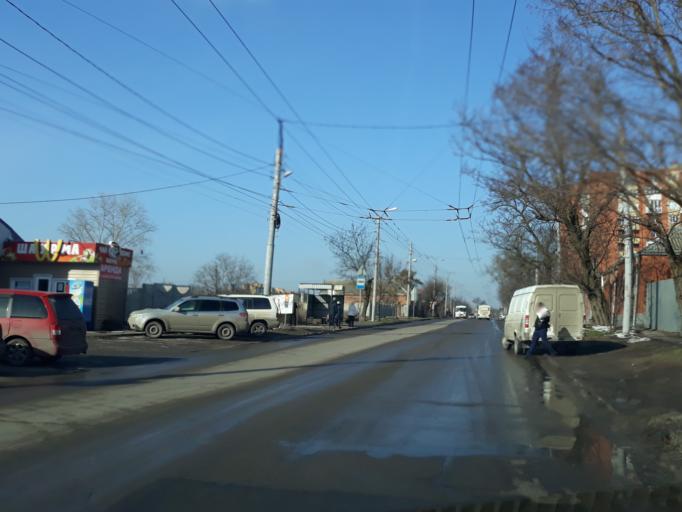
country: RU
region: Rostov
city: Taganrog
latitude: 47.2013
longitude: 38.9081
